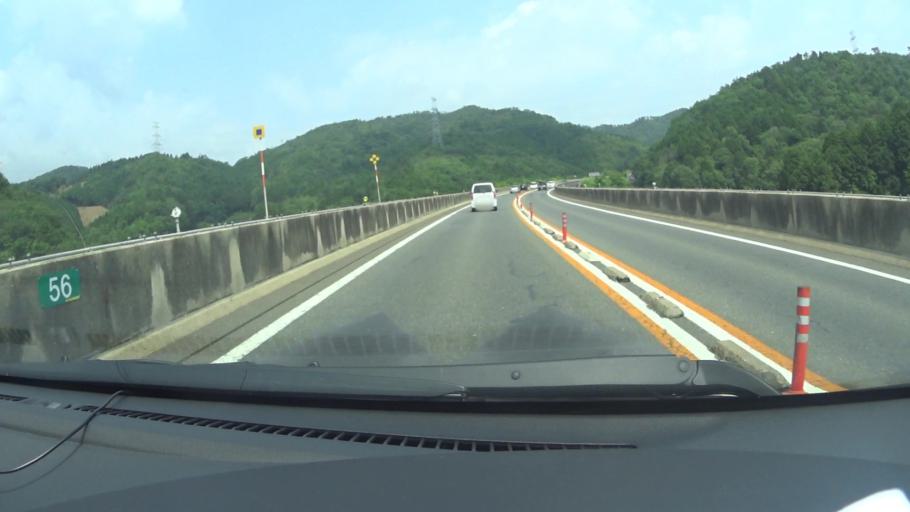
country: JP
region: Kyoto
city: Kameoka
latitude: 35.1285
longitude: 135.4604
